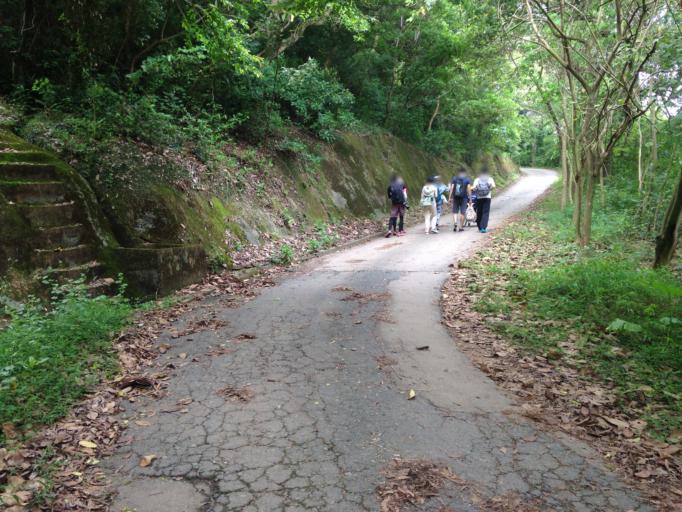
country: HK
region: Tsuen Wan
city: Tsuen Wan
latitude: 22.4199
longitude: 114.0907
